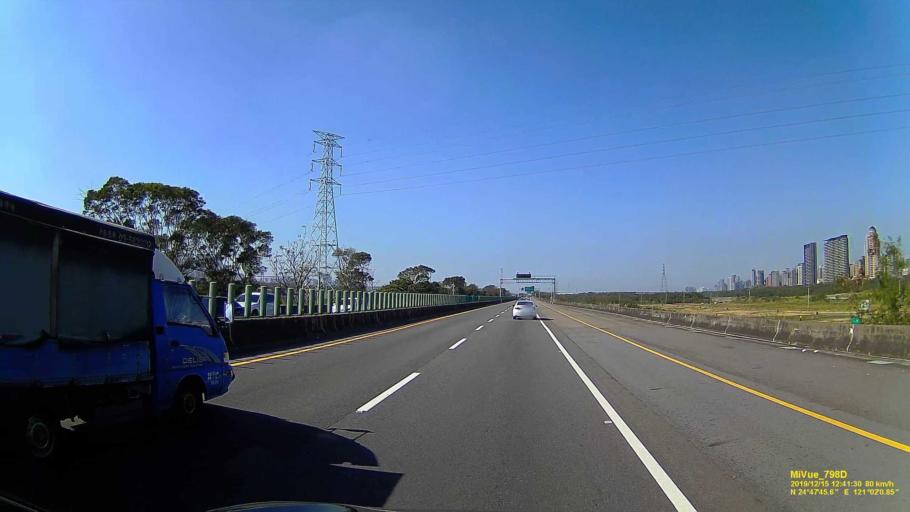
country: TW
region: Taiwan
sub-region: Hsinchu
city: Zhubei
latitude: 24.7958
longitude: 121.0333
